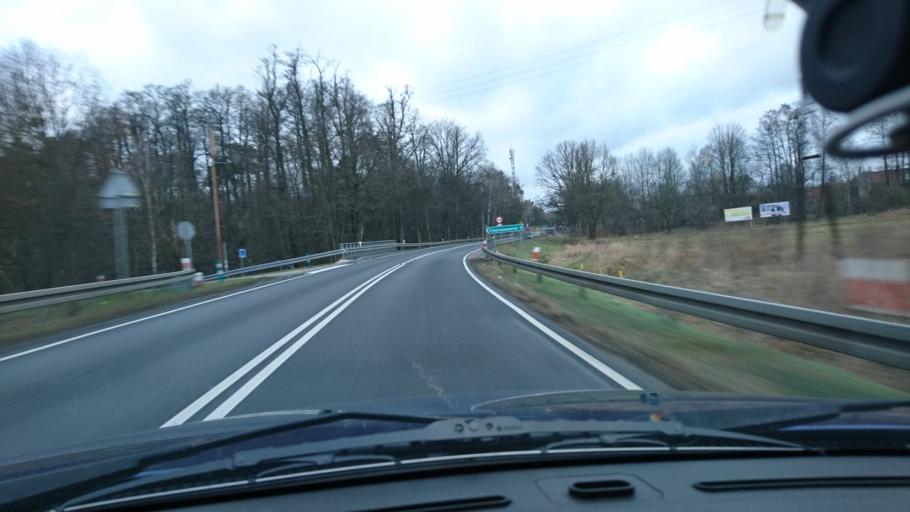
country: PL
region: Opole Voivodeship
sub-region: Powiat kluczborski
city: Kluczbork
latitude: 50.9544
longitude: 18.3089
